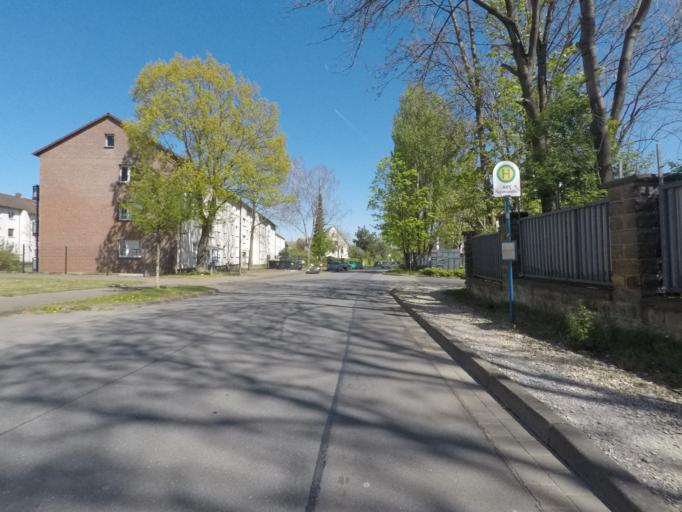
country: DE
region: North Rhine-Westphalia
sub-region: Regierungsbezirk Detmold
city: Bielefeld
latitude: 52.0146
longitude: 8.5703
